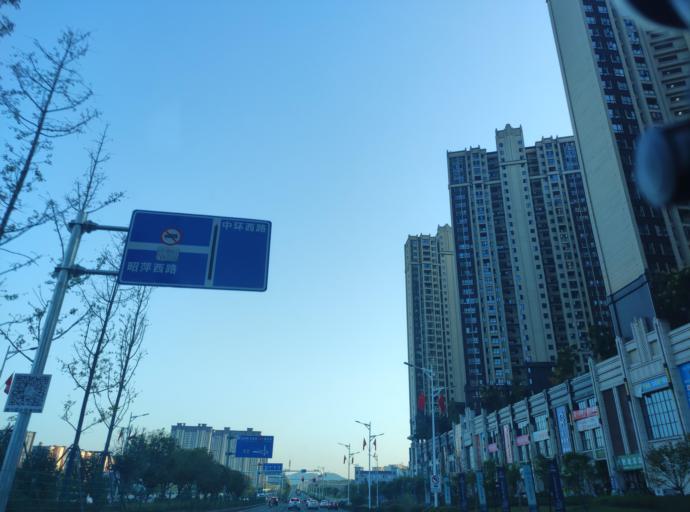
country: CN
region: Jiangxi Sheng
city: Pingxiang
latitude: 27.6326
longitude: 113.8296
